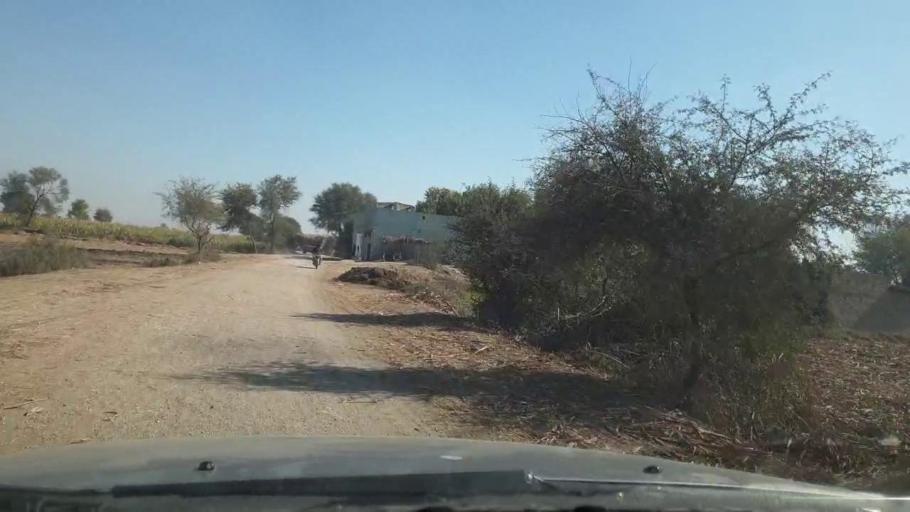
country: PK
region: Sindh
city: Ghotki
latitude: 28.0296
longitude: 69.2124
